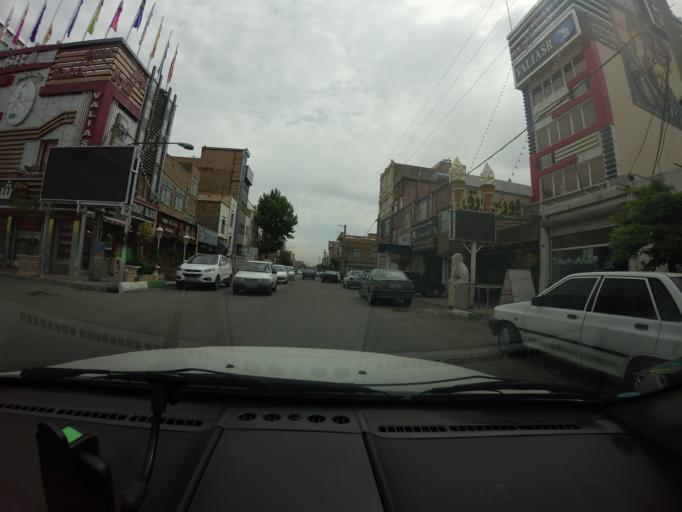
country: IR
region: Tehran
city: Eslamshahr
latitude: 35.5442
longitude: 51.2374
